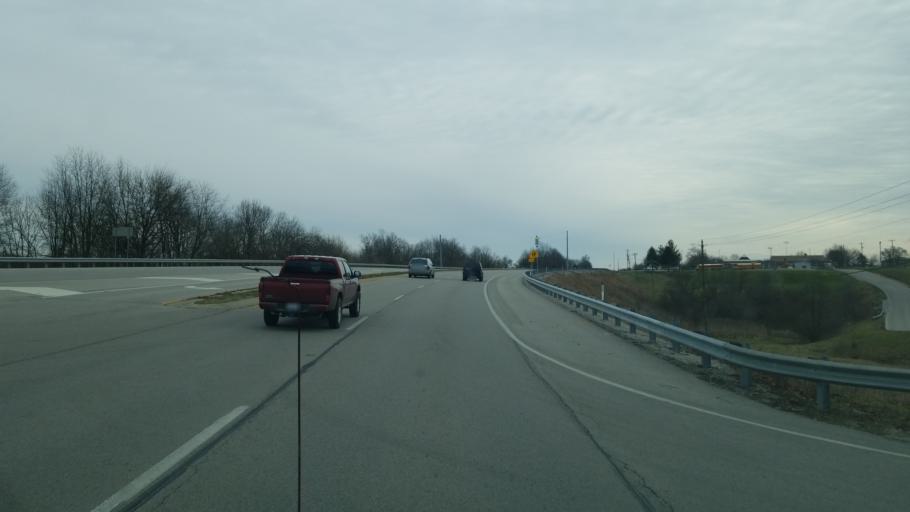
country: US
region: Kentucky
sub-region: Bourbon County
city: Paris
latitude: 38.2268
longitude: -84.2470
